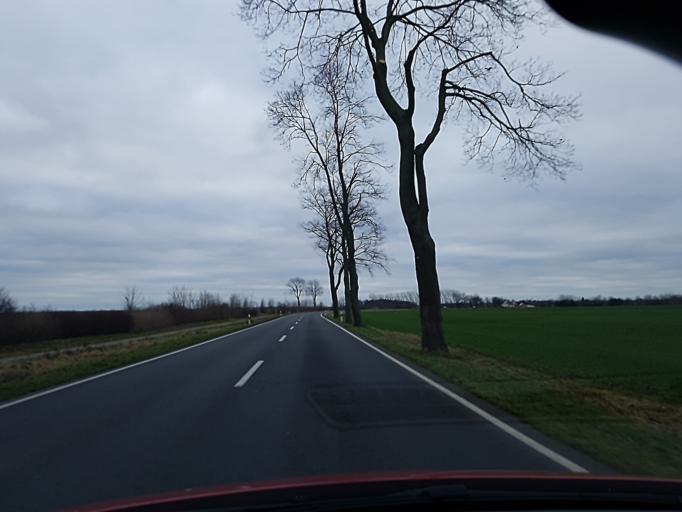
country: DE
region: Brandenburg
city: Elsterwerda
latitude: 51.4391
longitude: 13.5139
